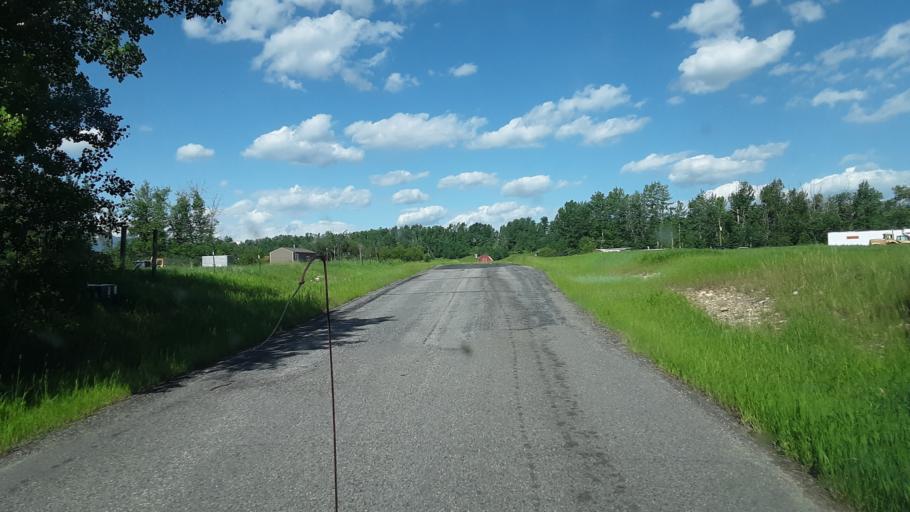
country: US
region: Montana
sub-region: Carbon County
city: Red Lodge
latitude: 45.2762
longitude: -109.2156
